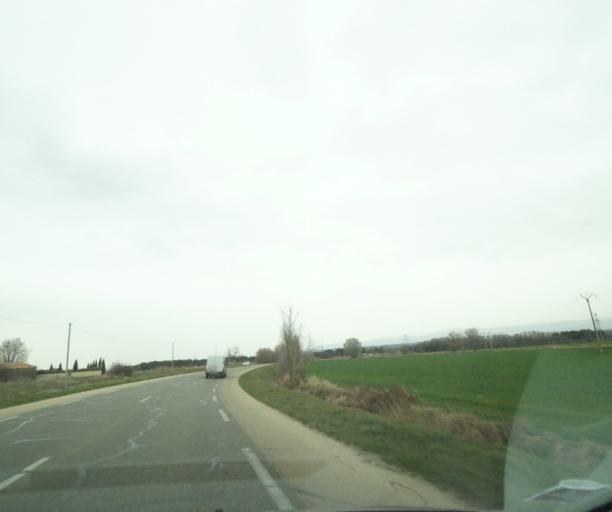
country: FR
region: Provence-Alpes-Cote d'Azur
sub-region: Departement des Bouches-du-Rhone
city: Meyrargues
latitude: 43.6551
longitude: 5.5094
